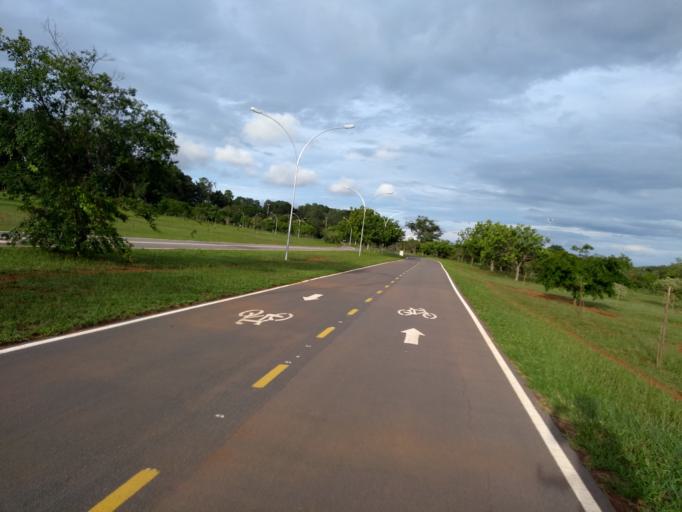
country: BR
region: Federal District
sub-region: Brasilia
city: Brasilia
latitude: -15.8089
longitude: -47.9242
